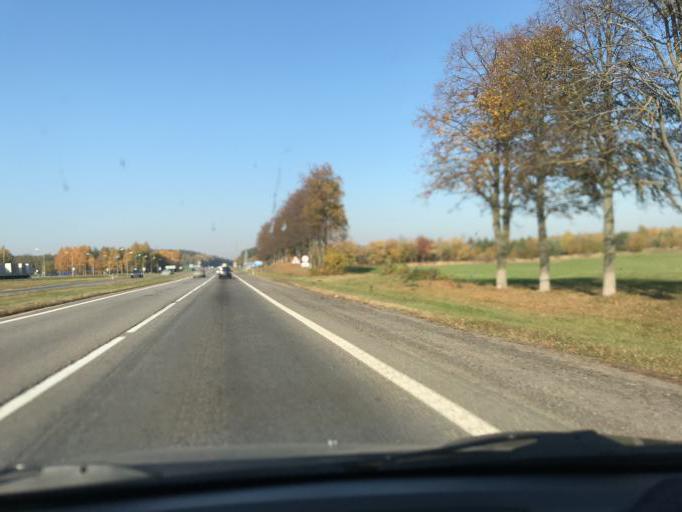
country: BY
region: Minsk
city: Luhavaya Slabada
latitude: 53.7553
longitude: 27.8314
